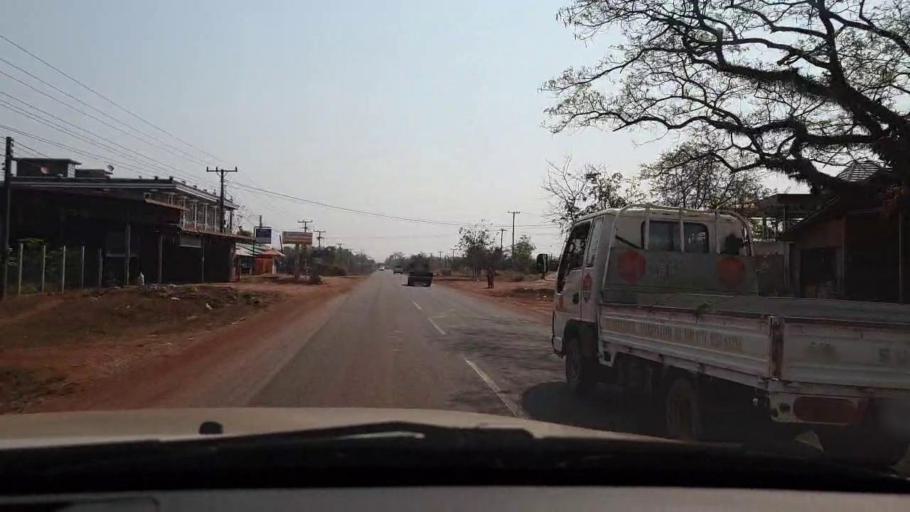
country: TH
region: Nong Khai
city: Nong Khai
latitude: 18.0542
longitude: 102.8377
